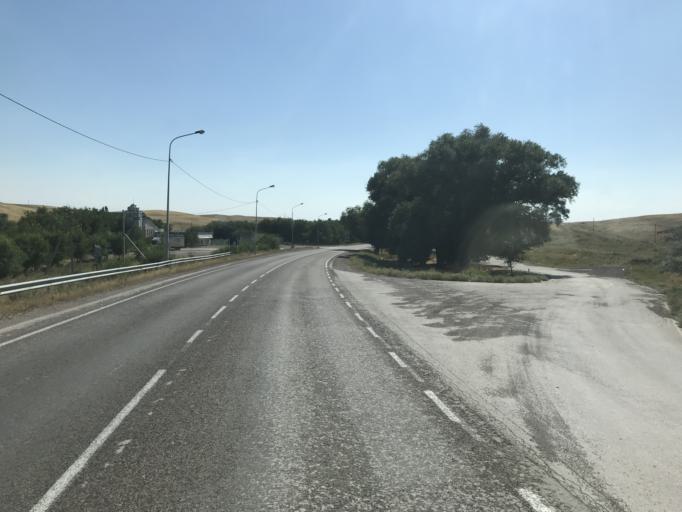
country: KZ
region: Zhambyl
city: Georgiyevka
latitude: 43.2415
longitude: 74.7773
